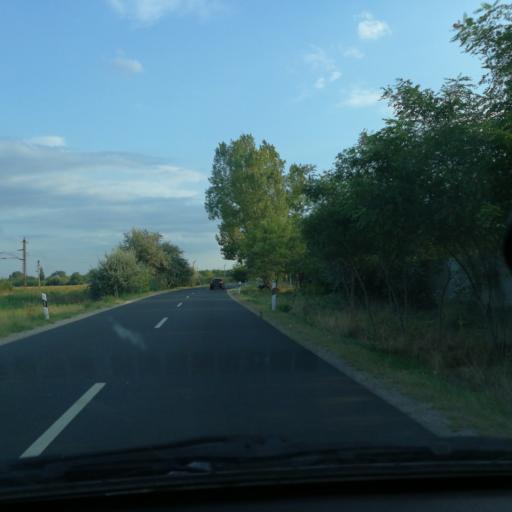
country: HU
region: Bacs-Kiskun
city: Jaszszentlaszlo
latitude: 46.6188
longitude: 19.7976
